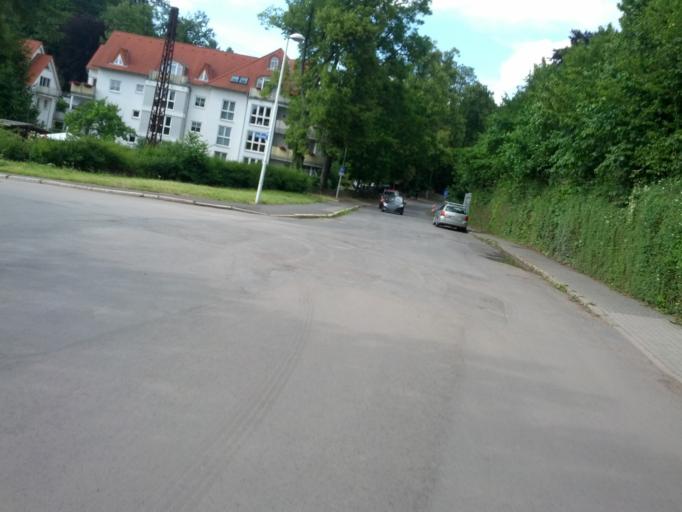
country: DE
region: Thuringia
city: Eisenach
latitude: 50.9811
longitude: 10.3331
